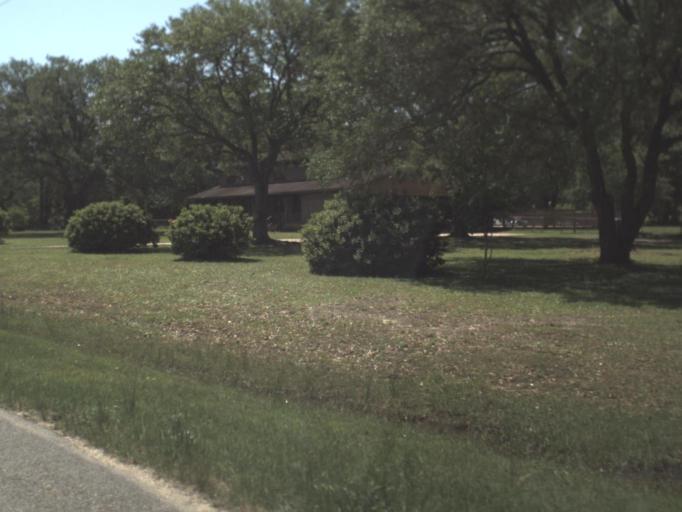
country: US
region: Florida
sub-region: Jackson County
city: Marianna
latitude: 30.6686
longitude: -85.2345
